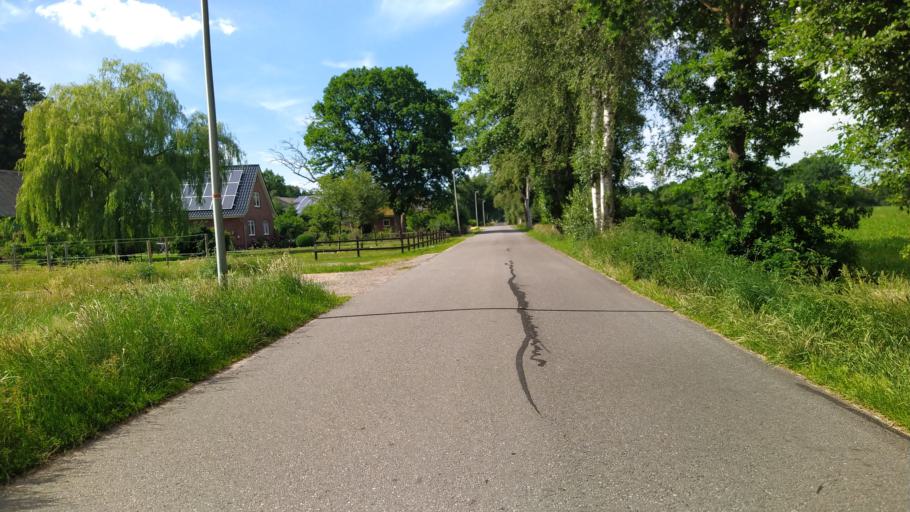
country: DE
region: Lower Saxony
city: Stinstedt
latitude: 53.6509
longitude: 8.9385
